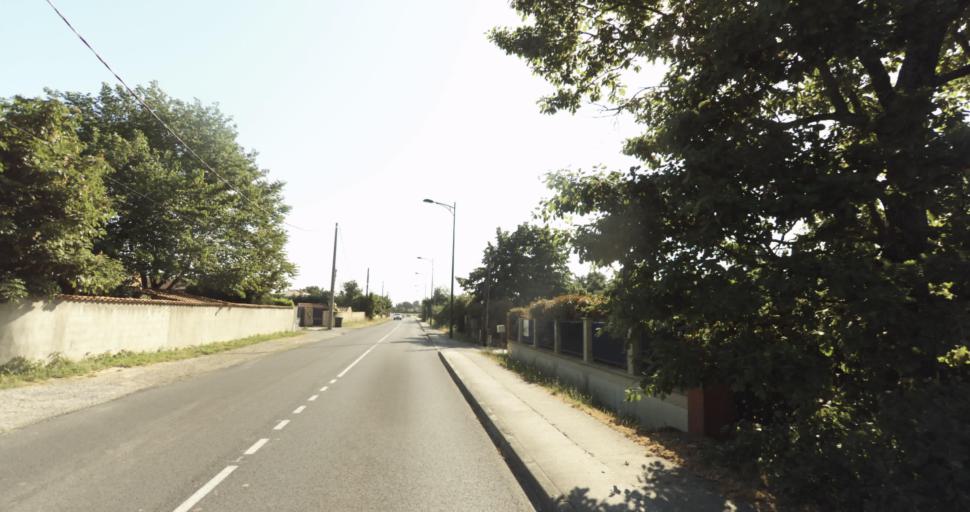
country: FR
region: Midi-Pyrenees
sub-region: Departement de la Haute-Garonne
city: La Salvetat-Saint-Gilles
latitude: 43.5641
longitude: 1.2684
